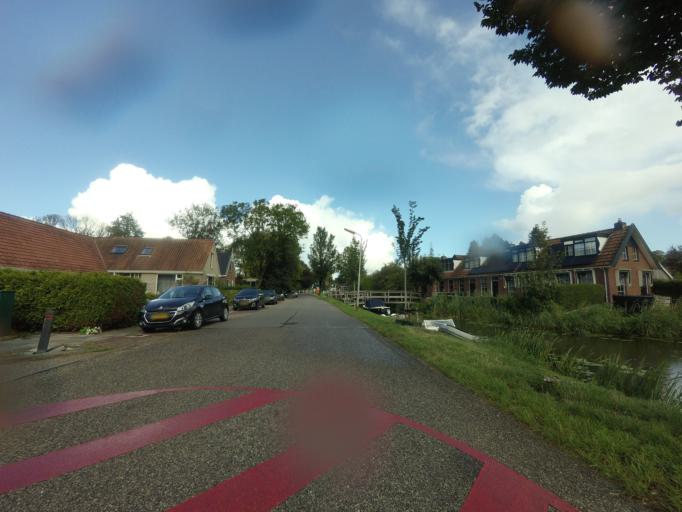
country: NL
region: Friesland
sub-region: Gemeente Leeuwarden
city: Wirdum
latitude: 53.1485
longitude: 5.8020
